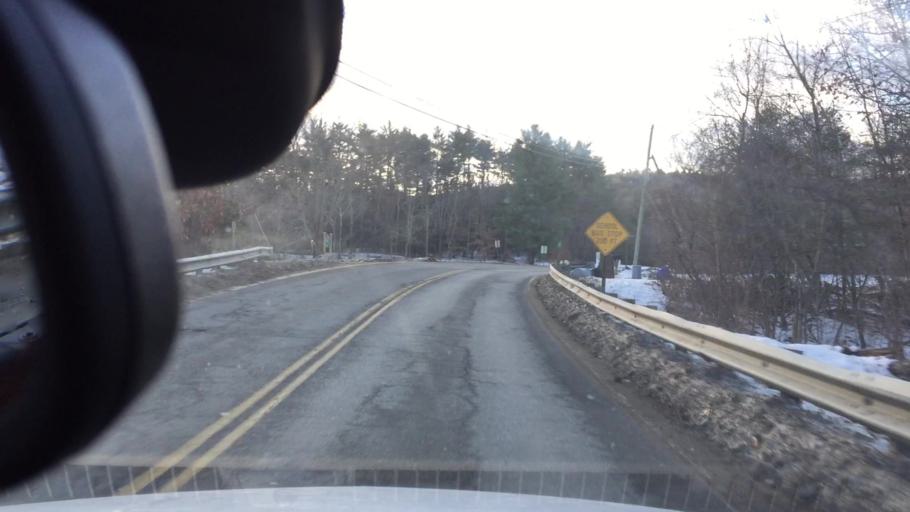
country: US
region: Massachusetts
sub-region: Franklin County
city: Montague
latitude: 42.5105
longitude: -72.5370
